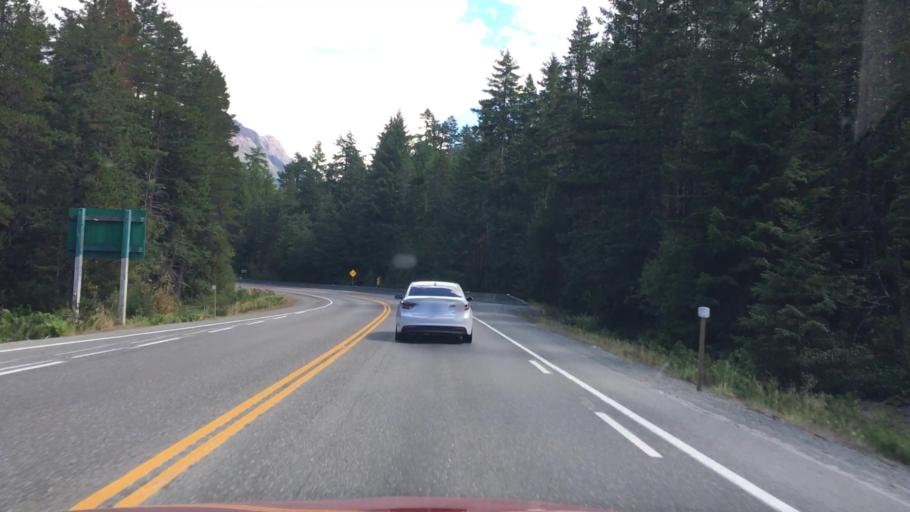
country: CA
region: British Columbia
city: Port Alberni
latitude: 49.2462
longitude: -124.6880
